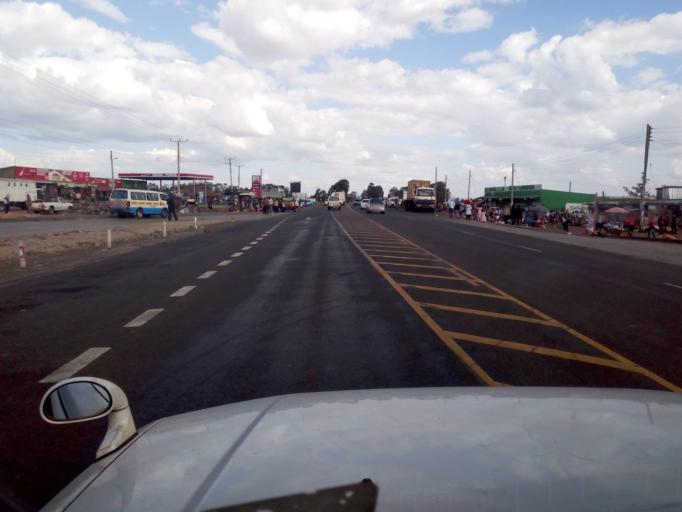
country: KE
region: Uasin Gishu
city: Eldoret
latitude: 0.3571
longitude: 35.3554
